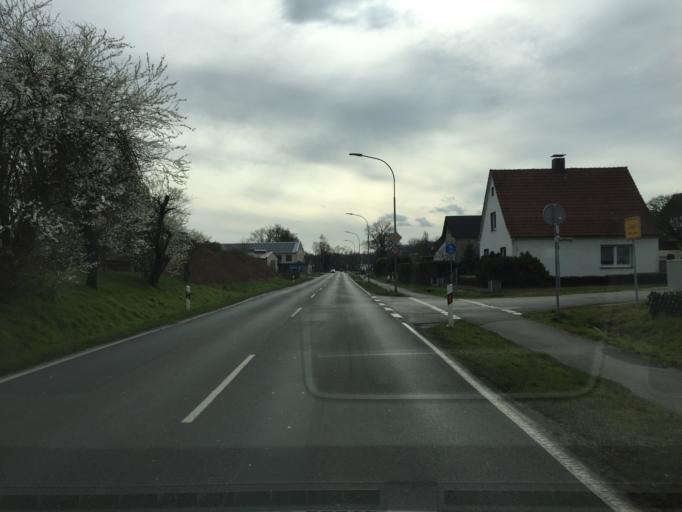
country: DE
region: North Rhine-Westphalia
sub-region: Regierungsbezirk Detmold
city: Lage
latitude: 51.9639
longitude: 8.8036
